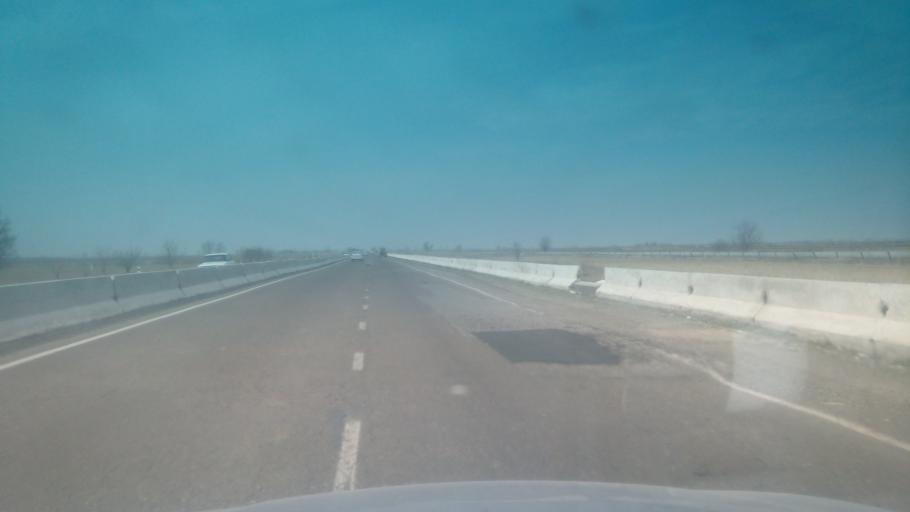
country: KZ
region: Ongtustik Qazaqstan
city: Myrzakent
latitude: 40.5044
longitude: 68.5187
